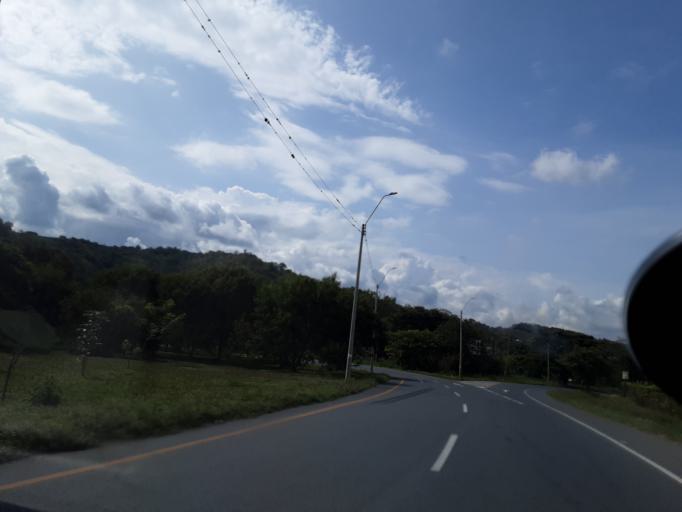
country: CO
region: Valle del Cauca
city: Buga
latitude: 3.8602
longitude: -76.2974
